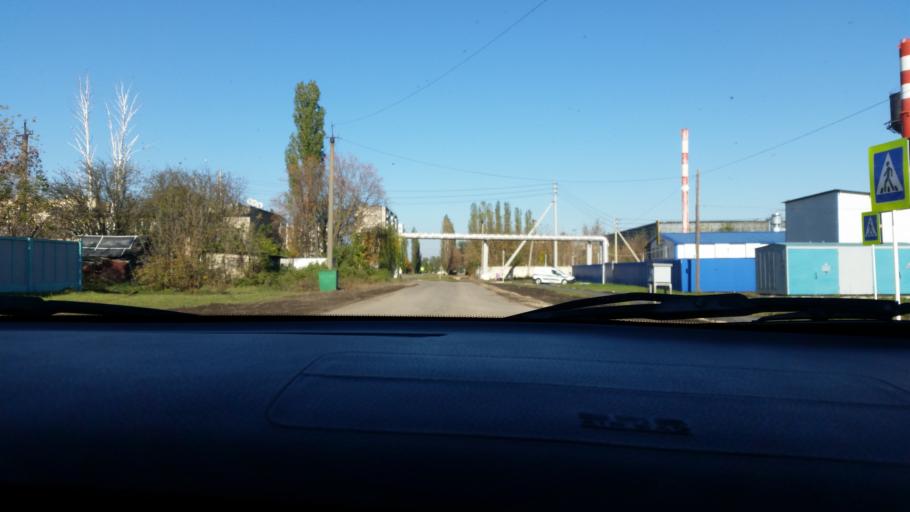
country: RU
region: Lipetsk
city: Gryazi
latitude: 52.4701
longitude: 39.9439
